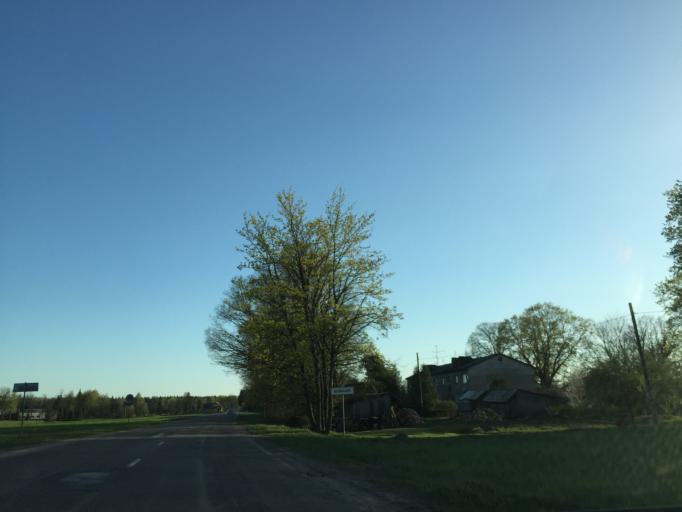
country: LV
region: Koknese
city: Koknese
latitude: 56.6812
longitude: 25.4854
